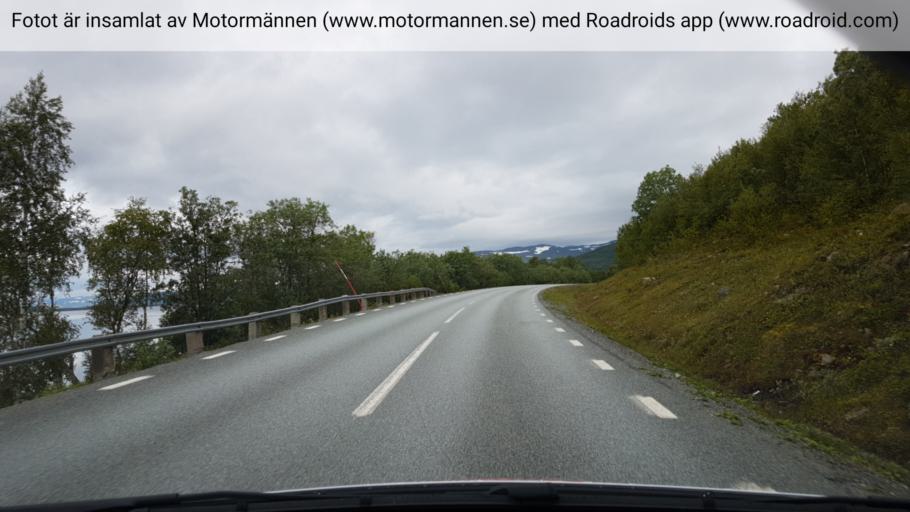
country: NO
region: Nordland
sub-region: Rana
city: Mo i Rana
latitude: 66.0847
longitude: 14.8617
